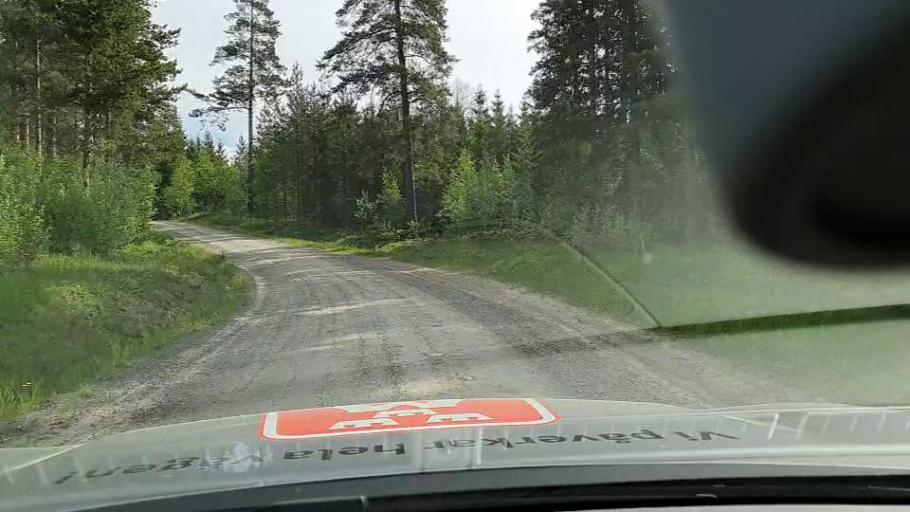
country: SE
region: Soedermanland
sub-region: Flens Kommun
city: Malmkoping
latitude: 59.2610
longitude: 16.8755
